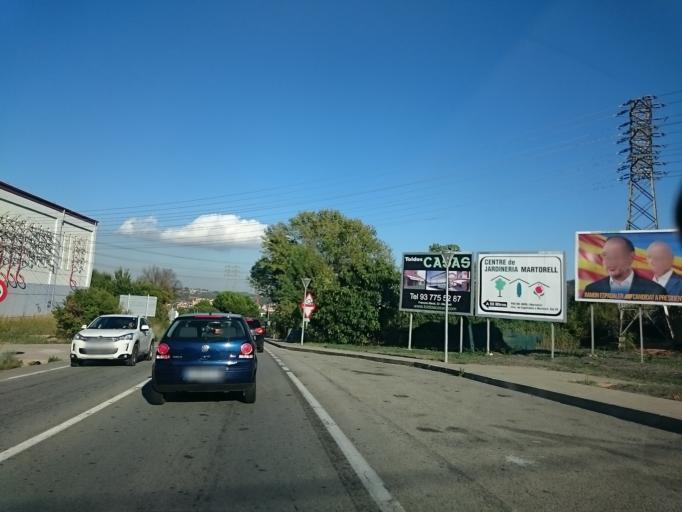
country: ES
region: Catalonia
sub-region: Provincia de Barcelona
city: Martorell
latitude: 41.4753
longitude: 1.9071
